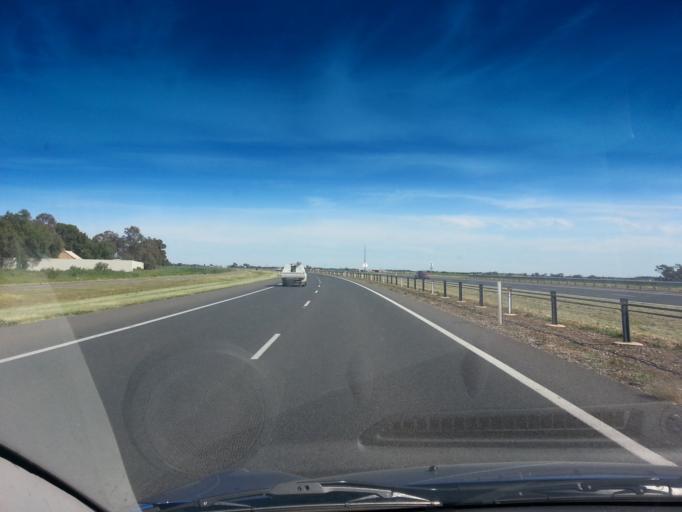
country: AU
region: South Australia
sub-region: Gawler
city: Gawler
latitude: -34.6018
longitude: 138.7122
